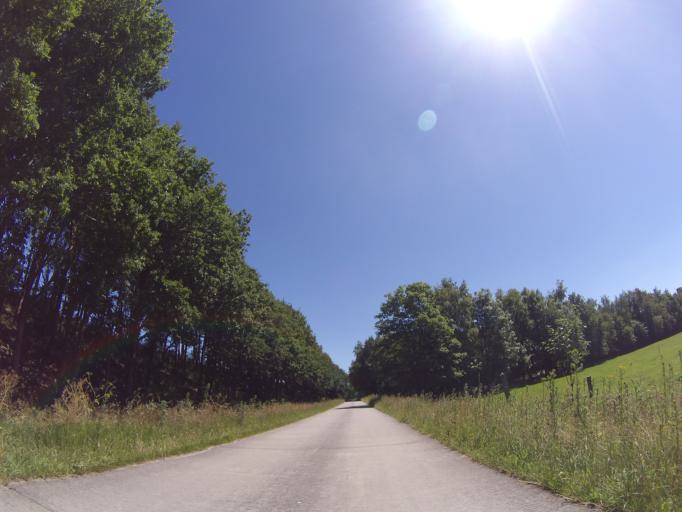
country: NL
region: Drenthe
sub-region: Gemeente Assen
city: Assen
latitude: 52.9684
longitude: 6.5640
